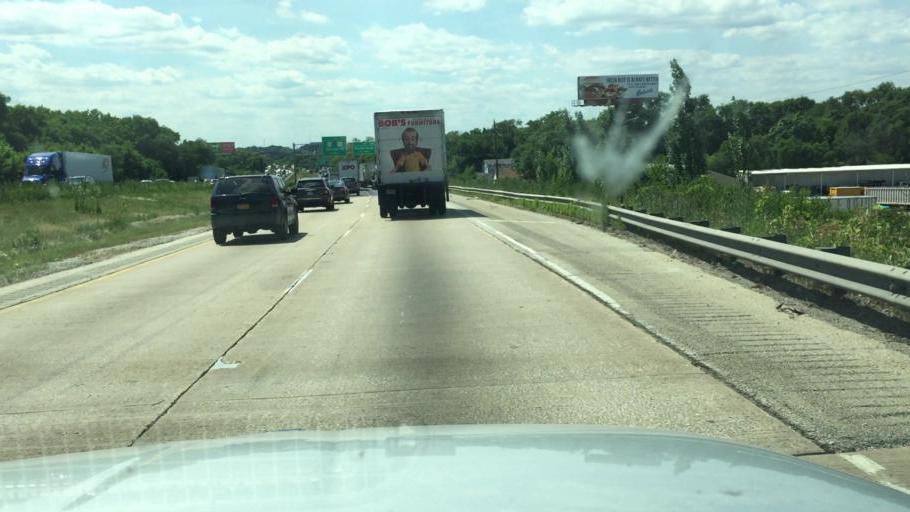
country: US
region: Illinois
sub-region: Will County
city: Ingalls Park
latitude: 41.5135
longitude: -88.0624
